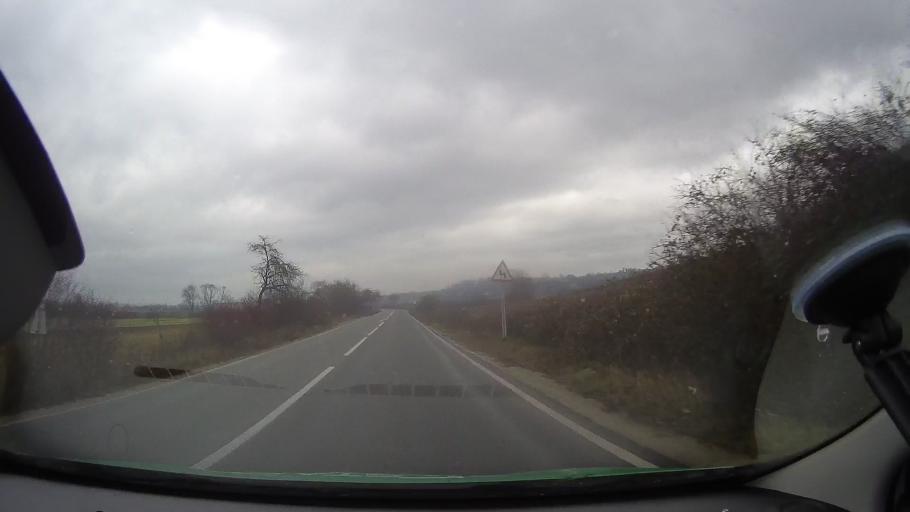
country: RO
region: Arad
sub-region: Comuna Almas
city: Almas
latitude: 46.2949
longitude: 22.2068
